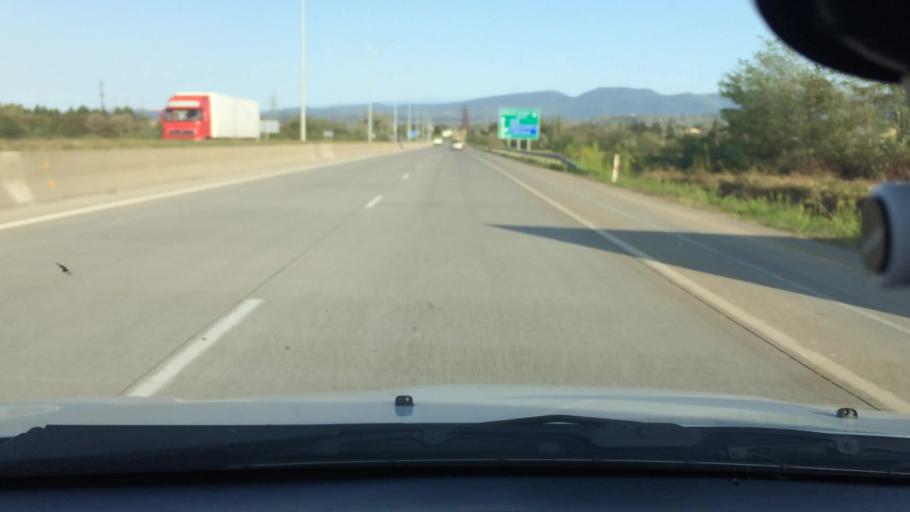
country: GE
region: Imereti
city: Zestap'oni
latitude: 42.1503
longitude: 42.9611
